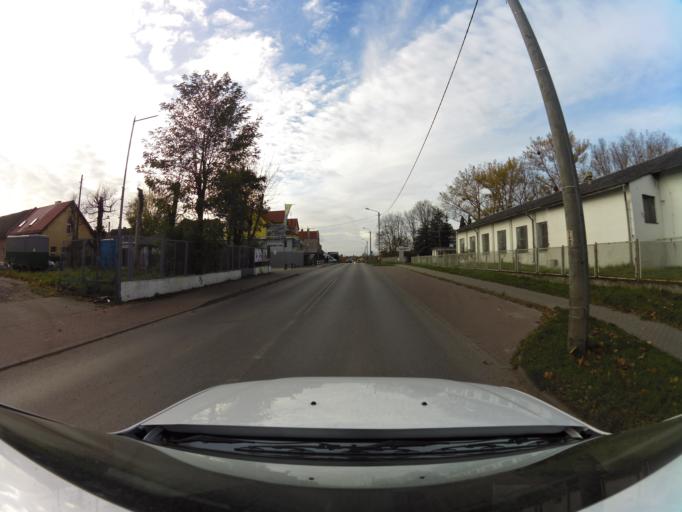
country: PL
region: West Pomeranian Voivodeship
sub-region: Powiat gryficki
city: Gryfice
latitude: 53.9199
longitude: 15.1941
